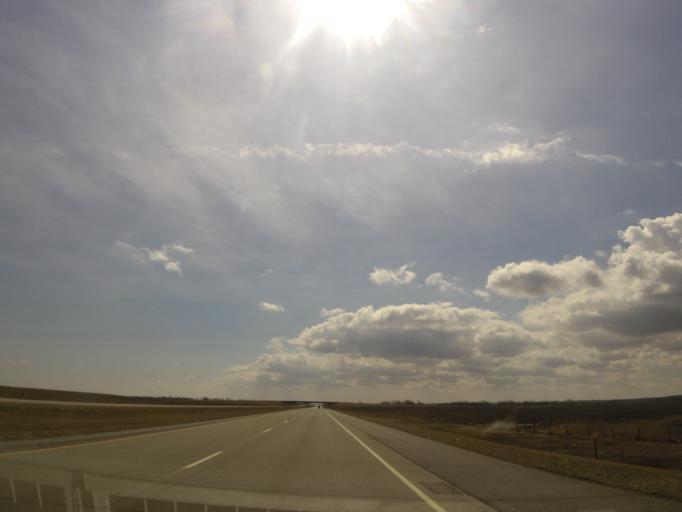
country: US
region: South Dakota
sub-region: Roberts County
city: Sisseton
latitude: 45.5228
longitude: -96.9897
